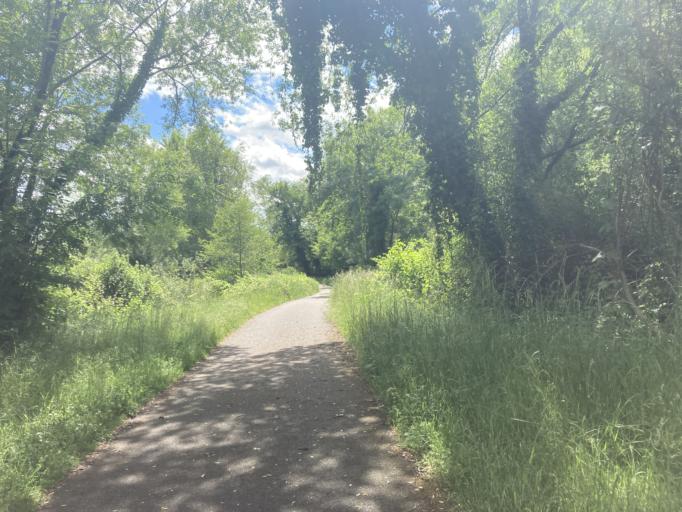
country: FR
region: Aquitaine
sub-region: Departement des Pyrenees-Atlantiques
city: Artiguelouve
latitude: 43.3285
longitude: -0.4626
